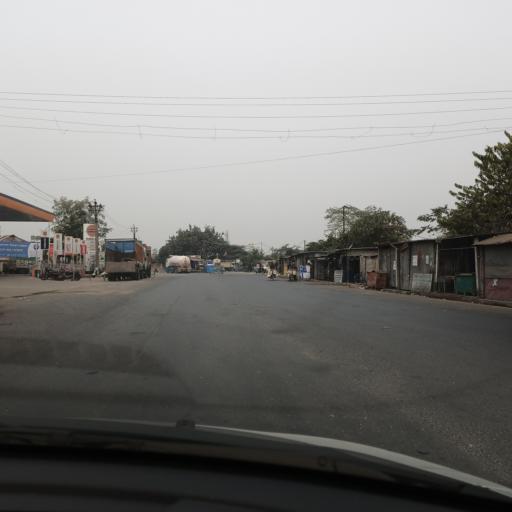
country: IN
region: West Bengal
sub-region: Darjiling
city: Shiliguri
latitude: 26.6571
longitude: 88.4156
